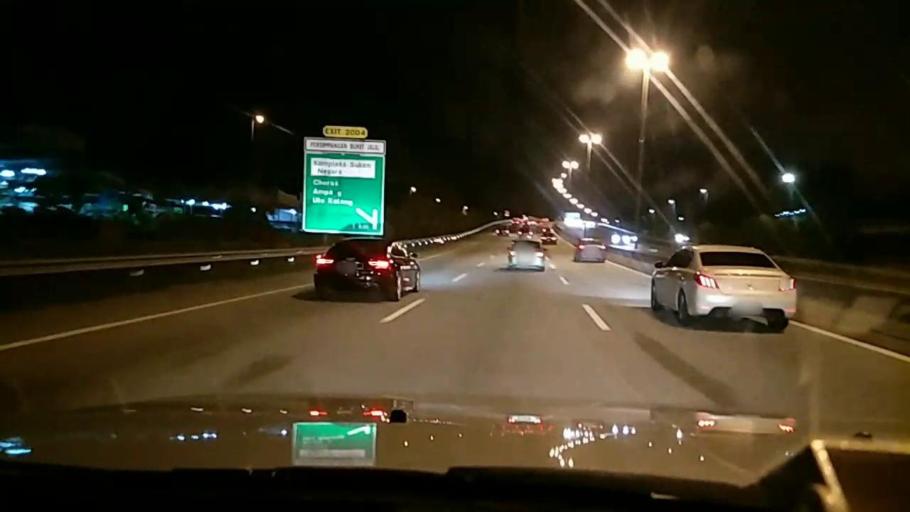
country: MY
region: Kuala Lumpur
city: Kuala Lumpur
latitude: 3.0769
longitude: 101.6905
